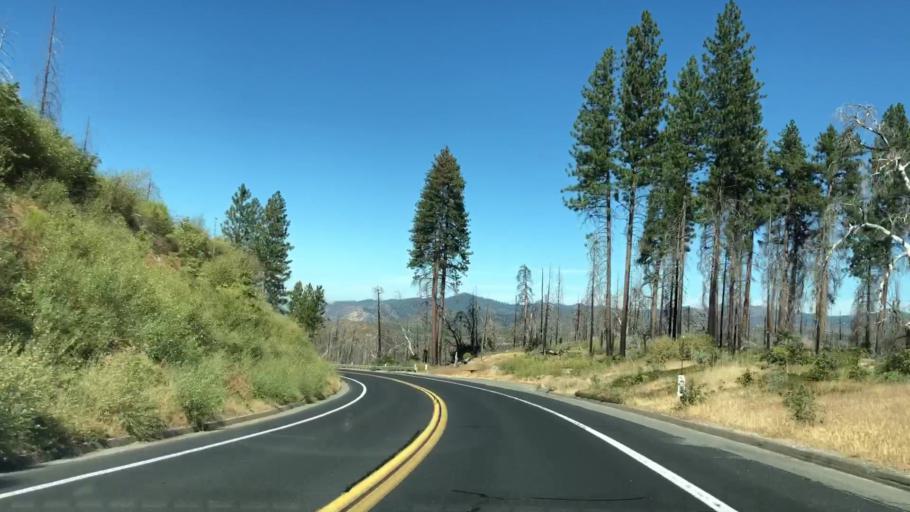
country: US
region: California
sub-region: Mariposa County
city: Midpines
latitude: 37.8269
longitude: -119.9742
